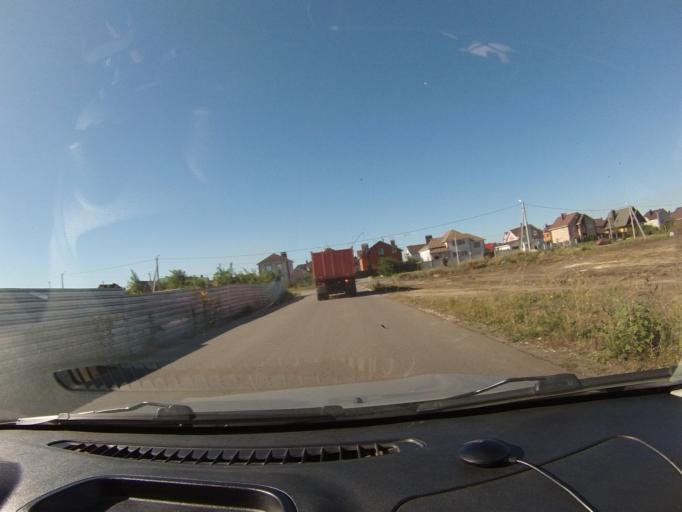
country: RU
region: Tambov
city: Tambov
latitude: 52.7651
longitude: 41.3860
